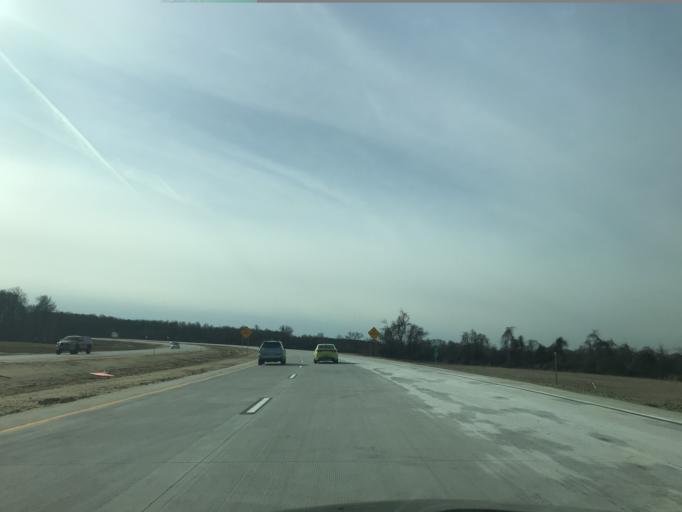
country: US
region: Delaware
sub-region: New Castle County
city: Middletown
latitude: 39.5219
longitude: -75.6888
